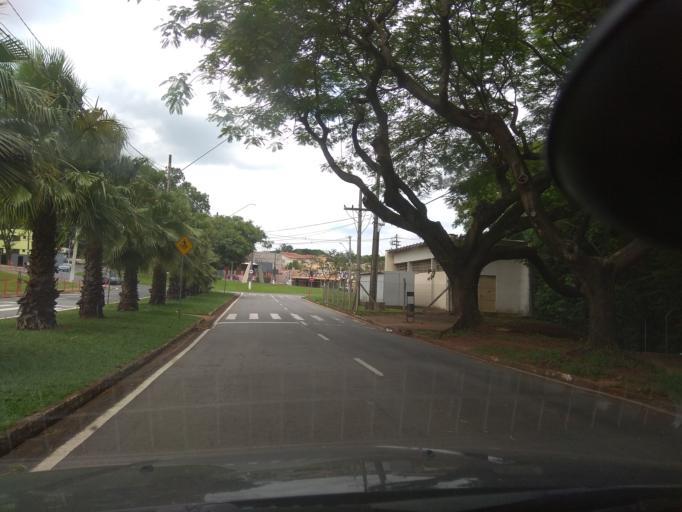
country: BR
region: Sao Paulo
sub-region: Campinas
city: Campinas
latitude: -22.8216
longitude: -47.0688
